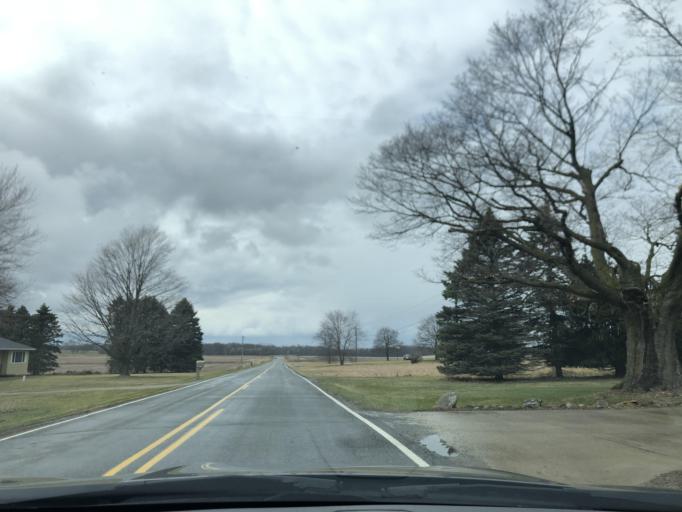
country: US
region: Michigan
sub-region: Clinton County
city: Saint Johns
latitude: 43.0605
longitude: -84.6029
